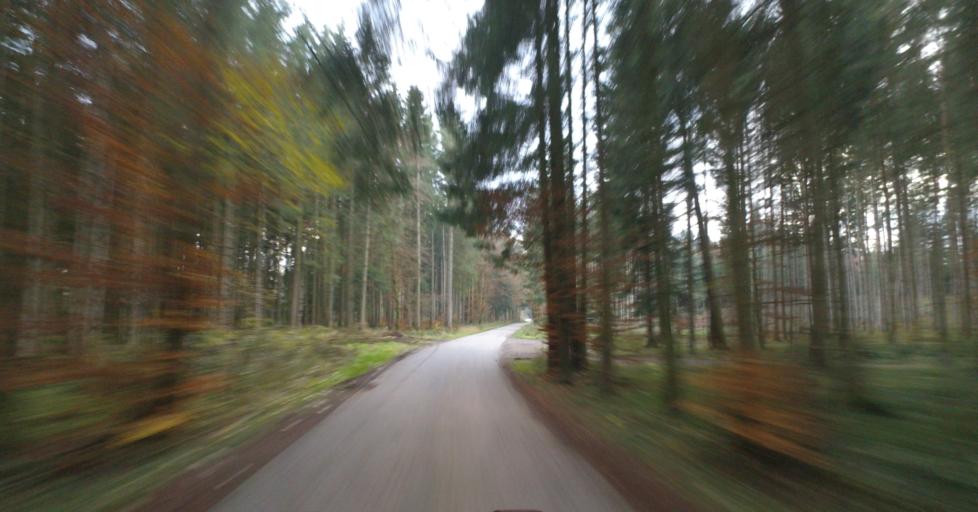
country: DE
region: Bavaria
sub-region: Upper Bavaria
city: Gstadt am Chiemsee
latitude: 47.9004
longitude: 12.4142
